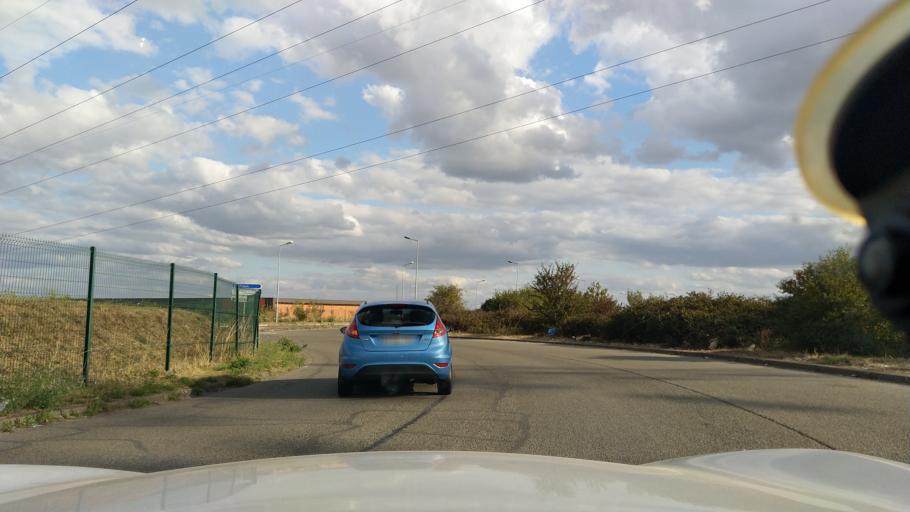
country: FR
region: Ile-de-France
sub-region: Departement du Val-d'Oise
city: Roissy-en-France
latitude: 48.9837
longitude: 2.5249
